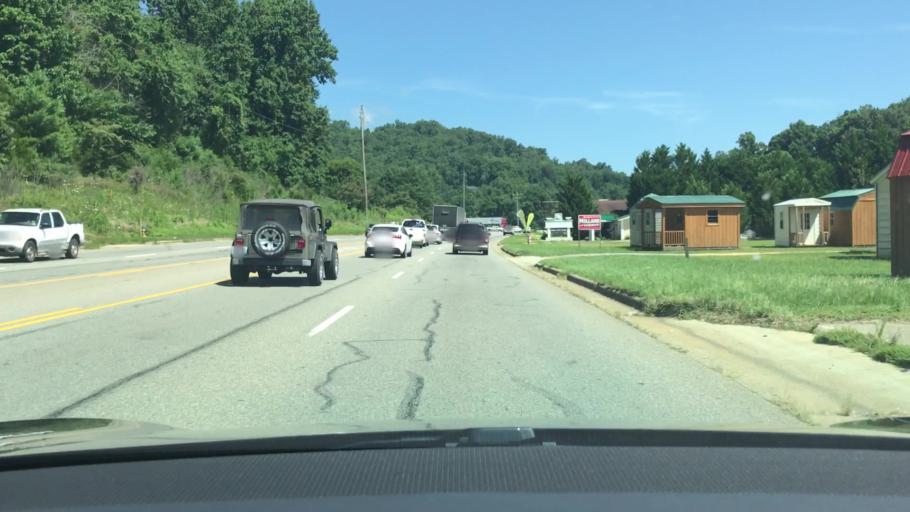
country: US
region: North Carolina
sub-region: Macon County
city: Franklin
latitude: 35.1360
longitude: -83.3978
